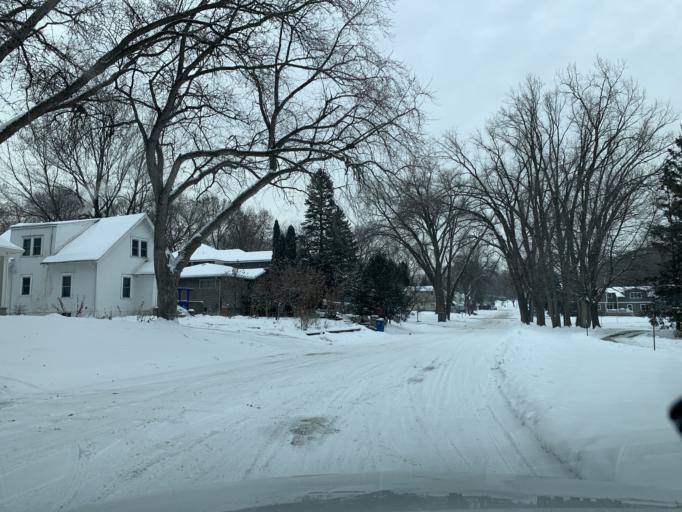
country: US
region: Minnesota
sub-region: Hennepin County
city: Edina
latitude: 44.9181
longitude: -93.3556
